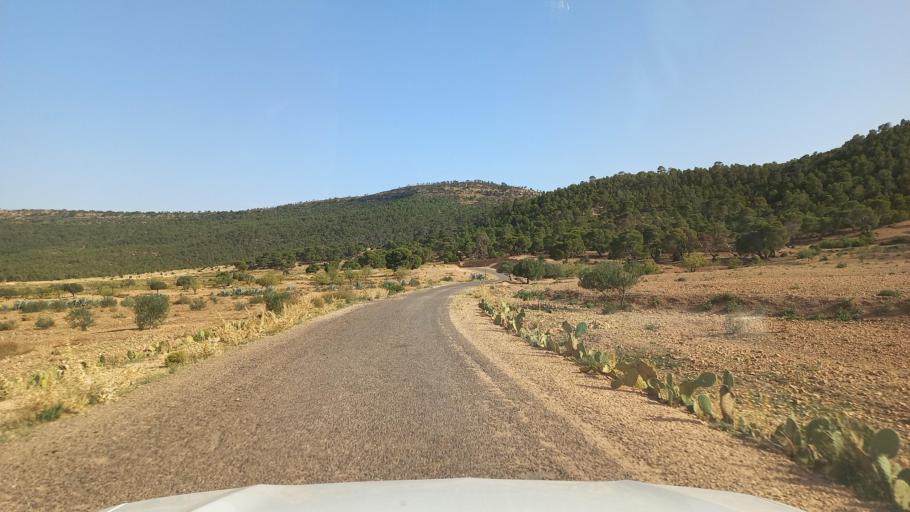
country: TN
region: Al Qasrayn
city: Kasserine
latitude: 35.3355
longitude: 8.8397
